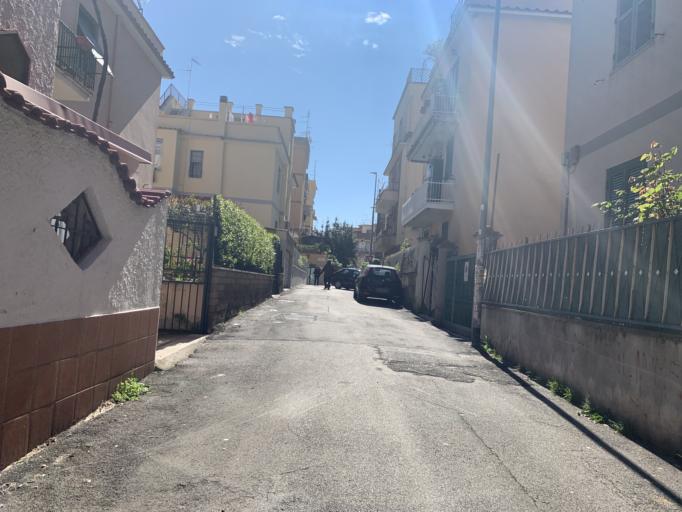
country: VA
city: Vatican City
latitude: 41.8827
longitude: 12.4202
